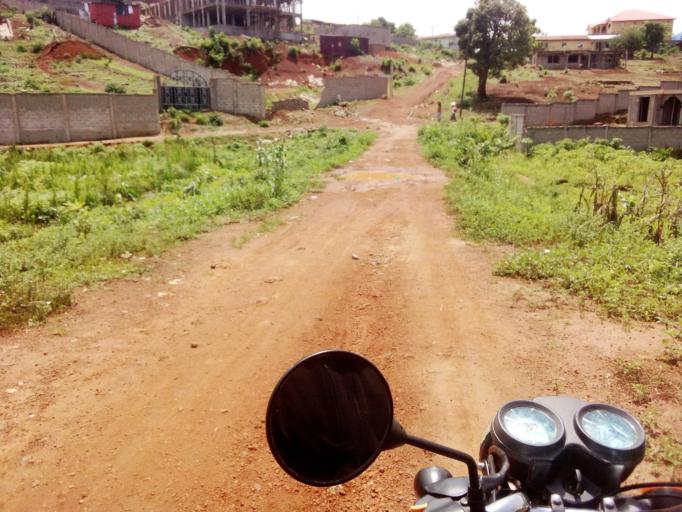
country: SL
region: Western Area
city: Waterloo
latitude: 8.3447
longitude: -13.0733
